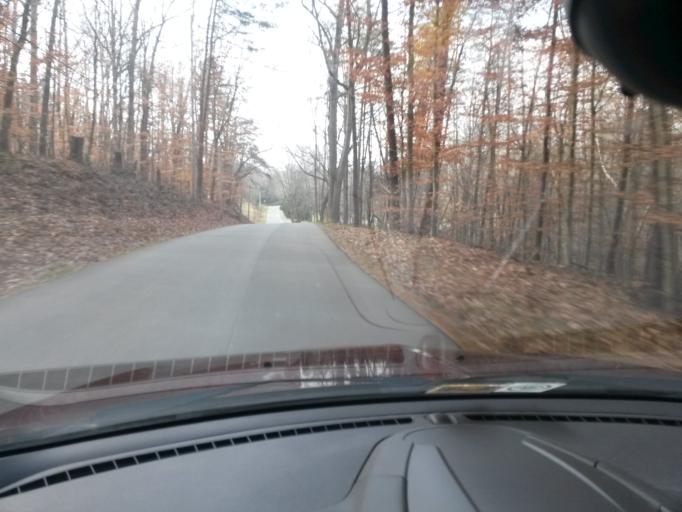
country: US
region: Virginia
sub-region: Botetourt County
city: Fincastle
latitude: 37.5873
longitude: -79.8677
